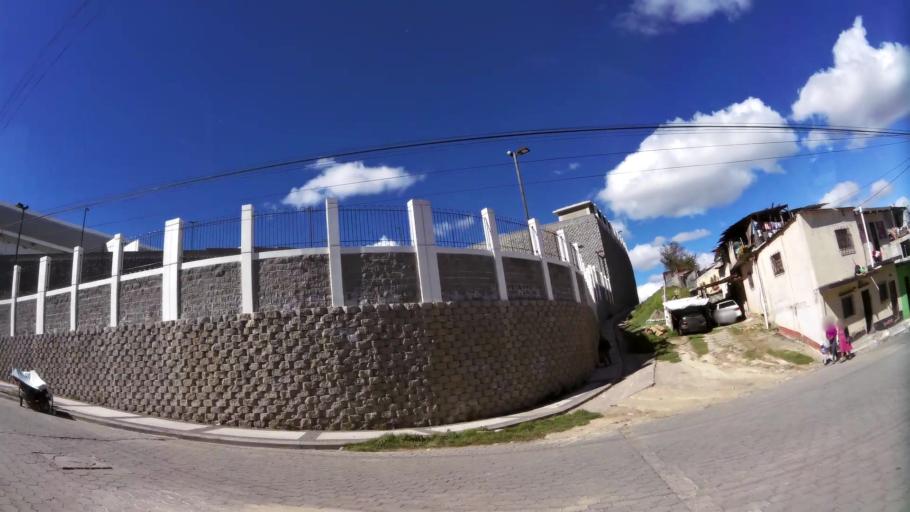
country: GT
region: Quetzaltenango
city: Quetzaltenango
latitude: 14.8379
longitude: -91.5020
